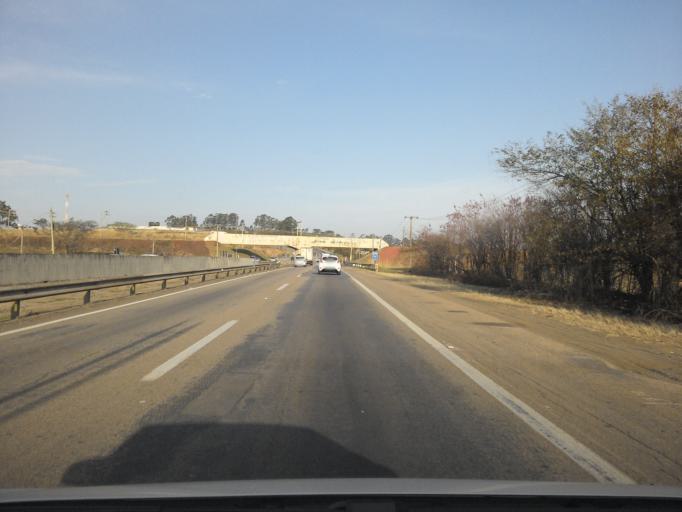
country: BR
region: Sao Paulo
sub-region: Campinas
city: Campinas
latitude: -22.8912
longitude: -47.1383
